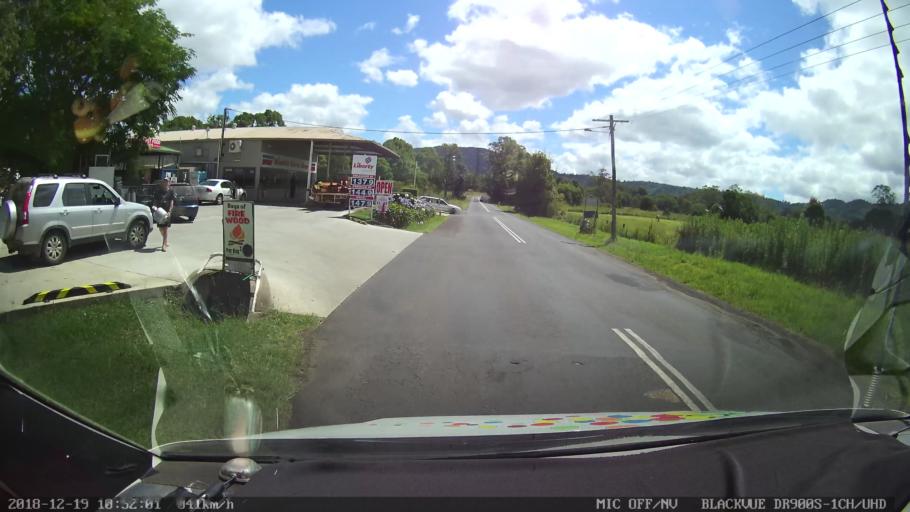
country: AU
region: New South Wales
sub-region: Lismore Municipality
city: Nimbin
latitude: -28.5935
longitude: 153.2266
